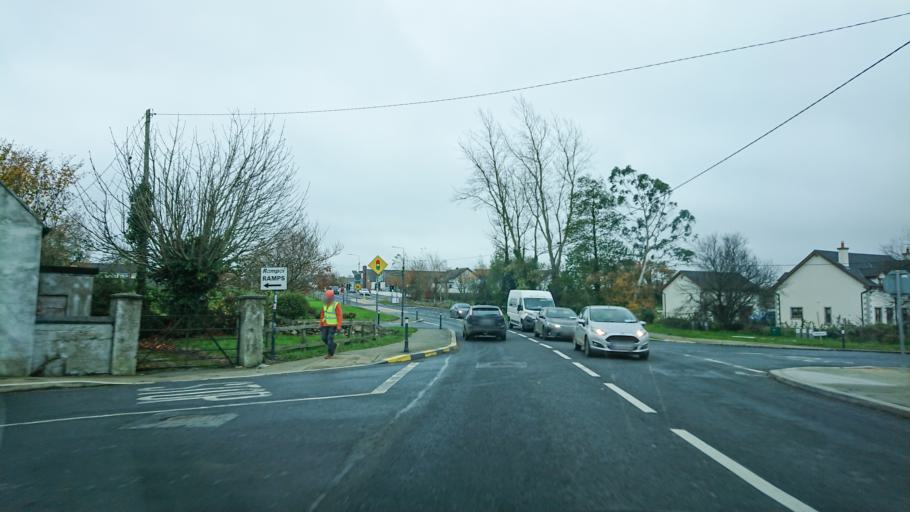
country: IE
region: Leinster
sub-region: Kilkenny
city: Mooncoin
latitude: 52.2915
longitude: -7.2521
